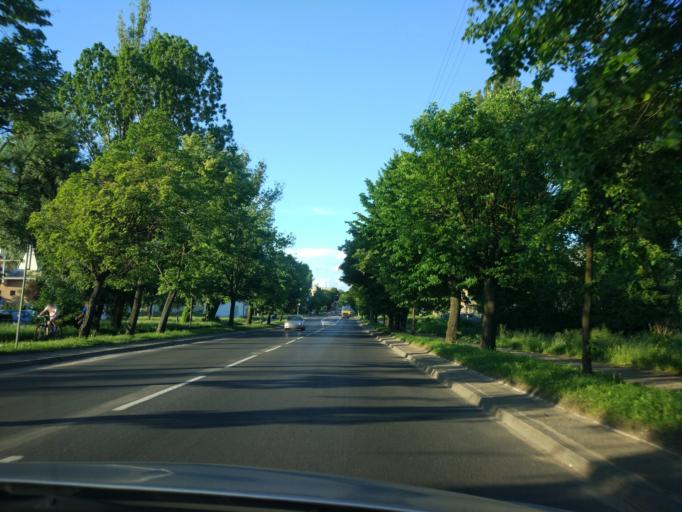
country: PL
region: Lodz Voivodeship
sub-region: Powiat kutnowski
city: Kutno
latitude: 52.2252
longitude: 19.3640
